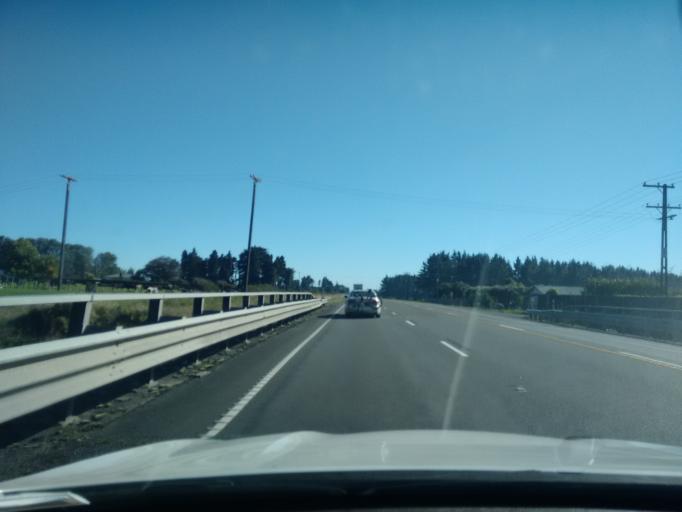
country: NZ
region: Taranaki
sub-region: South Taranaki District
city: Eltham
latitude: -39.2321
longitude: 174.2426
